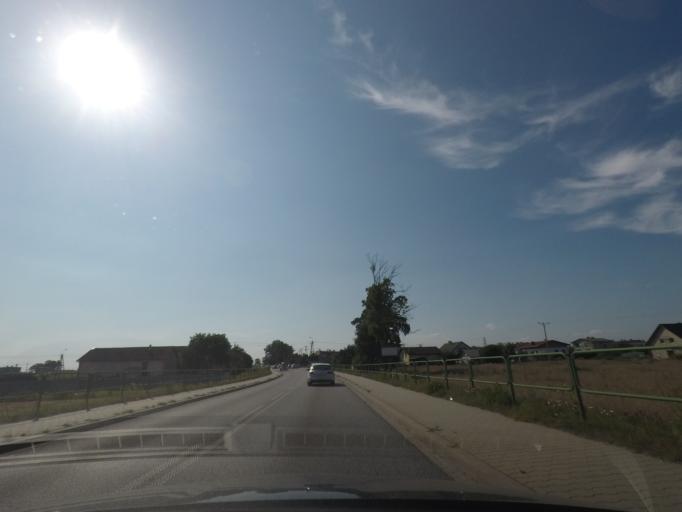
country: PL
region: Silesian Voivodeship
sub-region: Powiat pszczynski
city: Rudziczka
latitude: 50.0354
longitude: 18.7657
